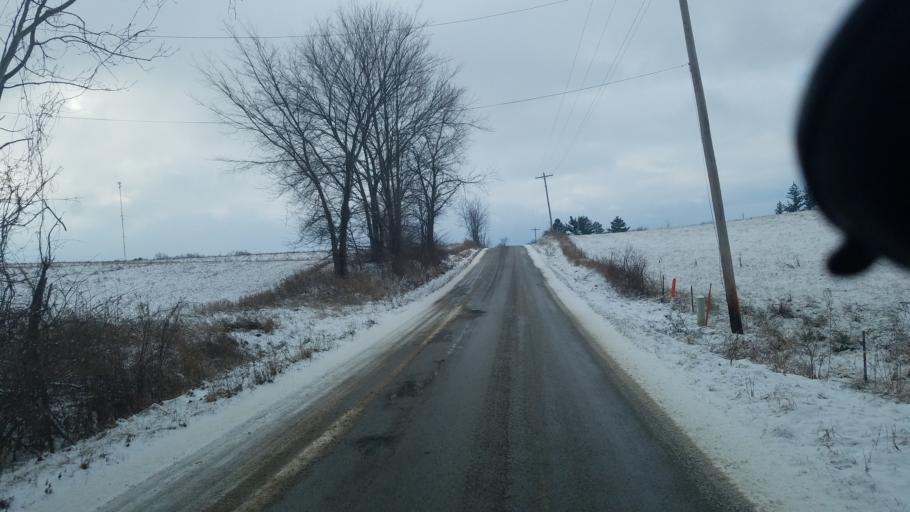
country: US
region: Ohio
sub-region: Morrow County
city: Mount Gilead
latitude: 40.5731
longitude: -82.8056
